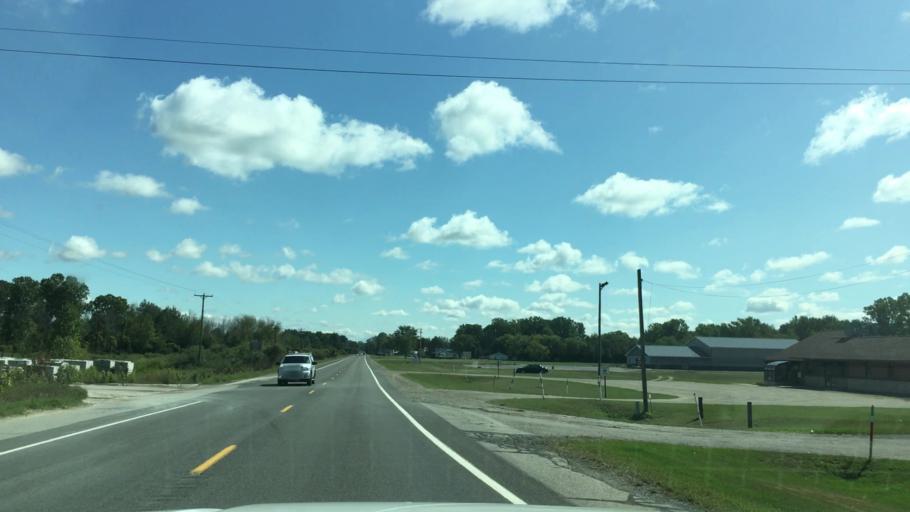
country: US
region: Michigan
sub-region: Montcalm County
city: Carson City
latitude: 43.1773
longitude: -84.8752
